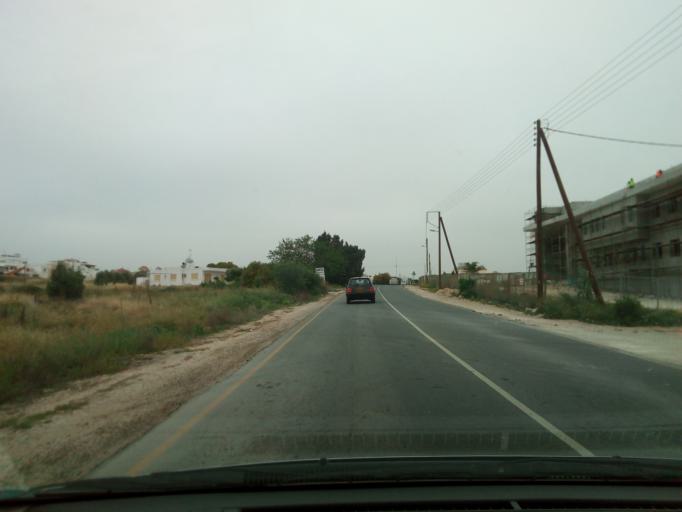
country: CY
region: Ammochostos
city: Paralimni
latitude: 35.0519
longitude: 33.9892
